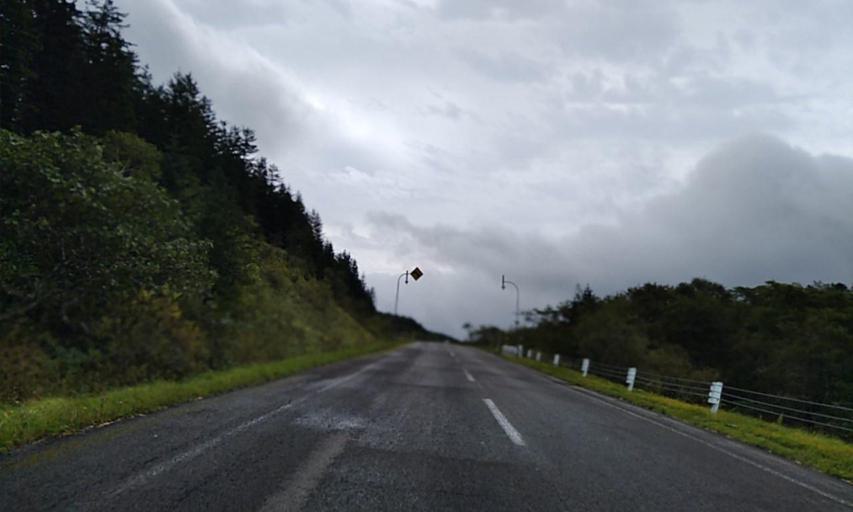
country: JP
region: Hokkaido
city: Abashiri
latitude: 43.6166
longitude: 144.5838
